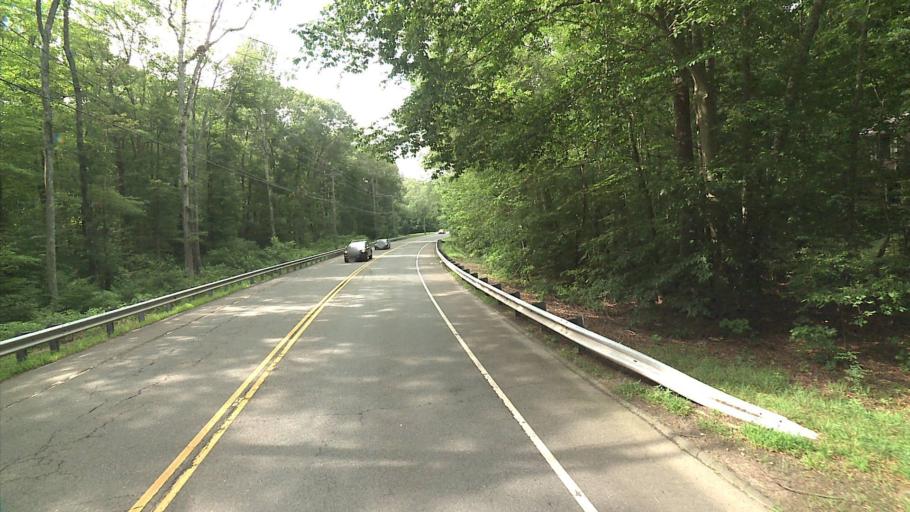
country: US
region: Connecticut
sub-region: Middlesex County
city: Clinton
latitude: 41.3293
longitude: -72.4914
